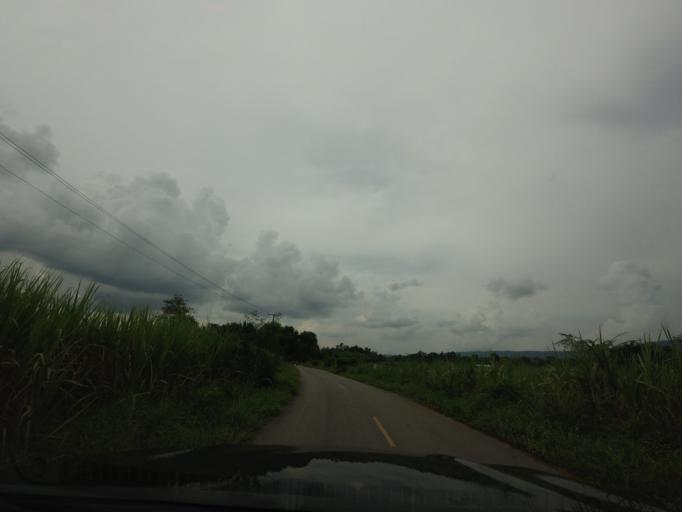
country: TH
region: Changwat Nong Bua Lamphu
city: Nong Bua Lamphu
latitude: 17.2608
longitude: 102.3879
